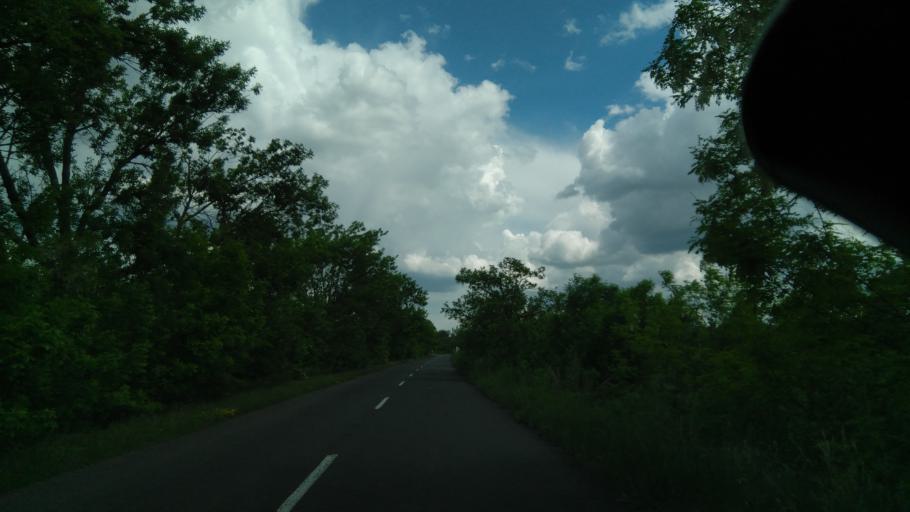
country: HU
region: Bekes
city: Korosladany
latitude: 46.9903
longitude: 21.0316
